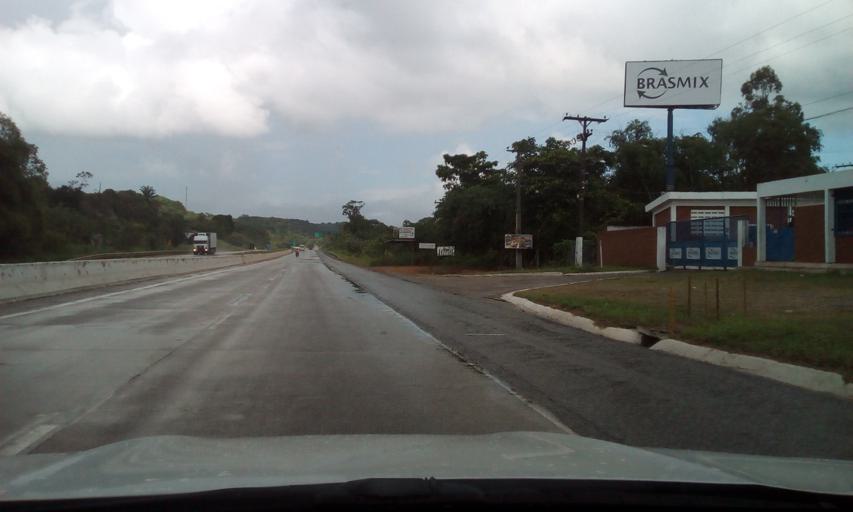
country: BR
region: Pernambuco
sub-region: Cabo De Santo Agostinho
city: Cabo
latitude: -8.3087
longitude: -35.0869
